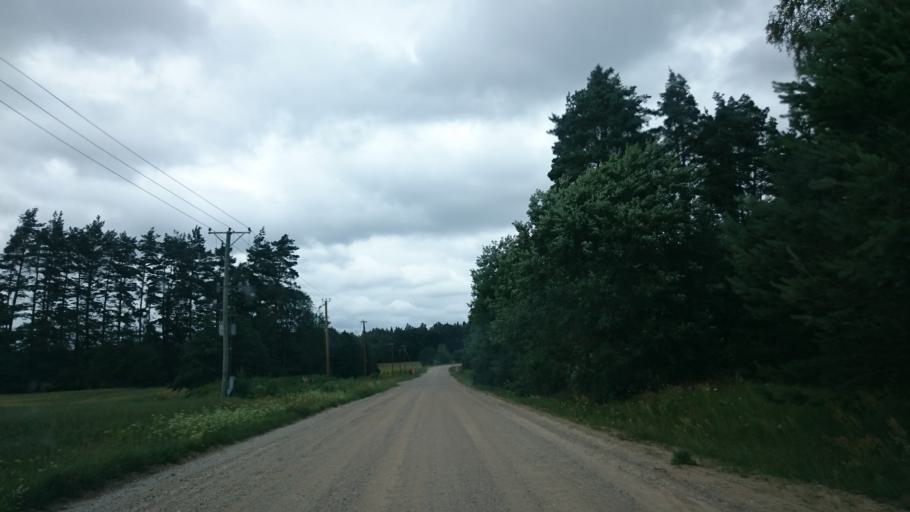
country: LV
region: Pavilostas
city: Pavilosta
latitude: 56.7661
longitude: 21.2775
